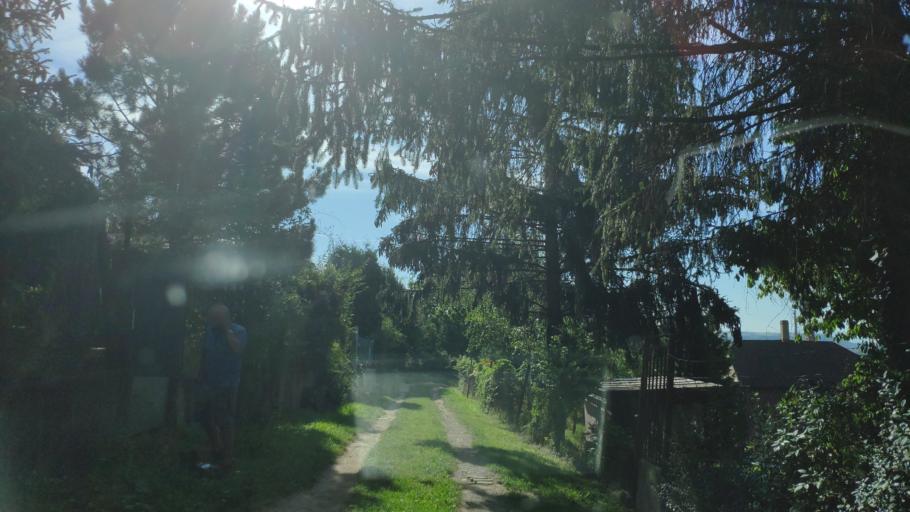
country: SK
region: Kosicky
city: Kosice
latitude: 48.7630
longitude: 21.2530
